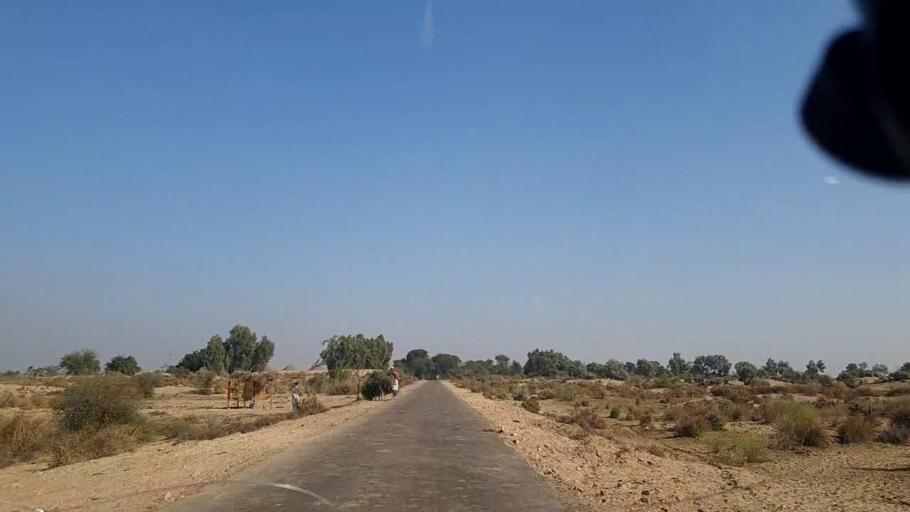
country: PK
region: Sindh
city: Khanpur
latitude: 27.6861
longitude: 69.4835
